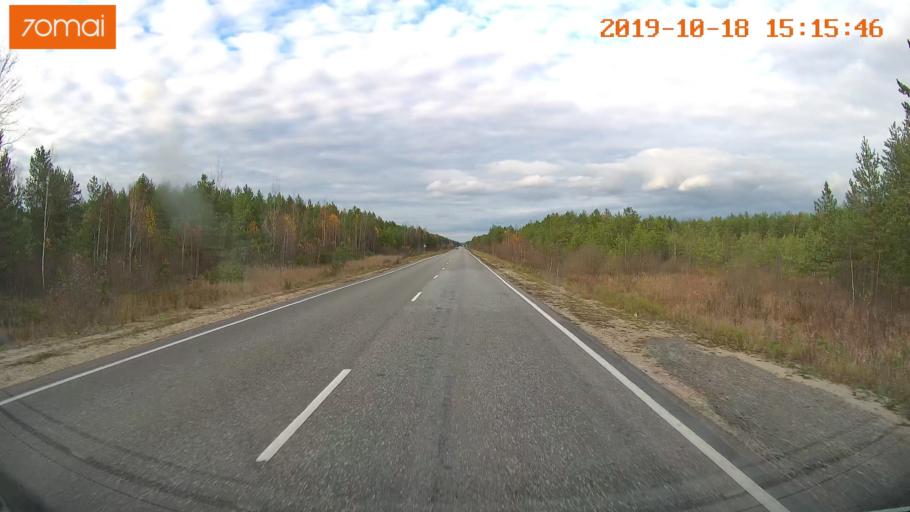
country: RU
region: Vladimir
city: Gus'-Khrustal'nyy
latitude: 55.6245
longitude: 40.7231
